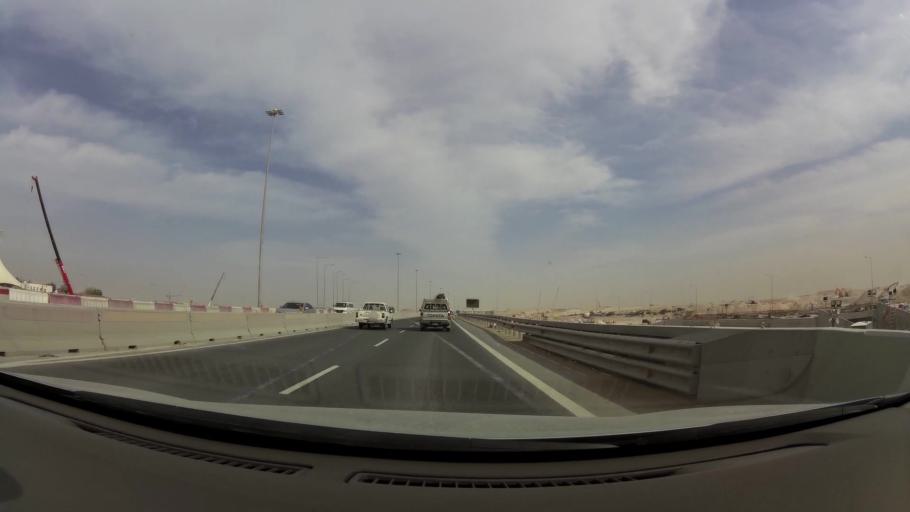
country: QA
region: Baladiyat ar Rayyan
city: Ash Shahaniyah
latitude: 25.3359
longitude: 51.3257
